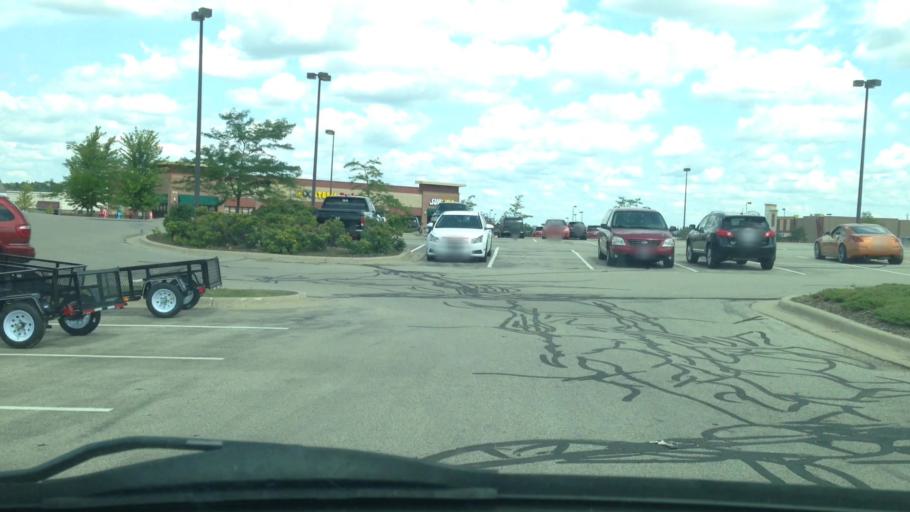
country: US
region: Minnesota
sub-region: Olmsted County
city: Rochester
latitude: 43.9544
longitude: -92.4610
